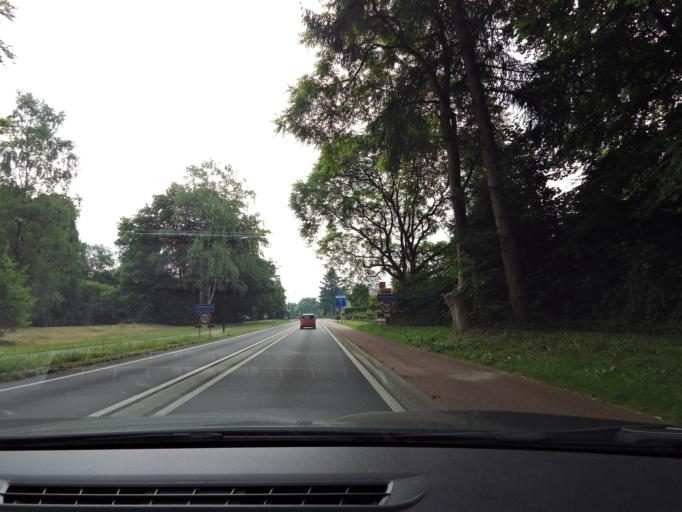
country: NL
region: Gelderland
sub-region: Gemeente Renkum
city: Doorwerth
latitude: 51.9877
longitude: 5.8182
